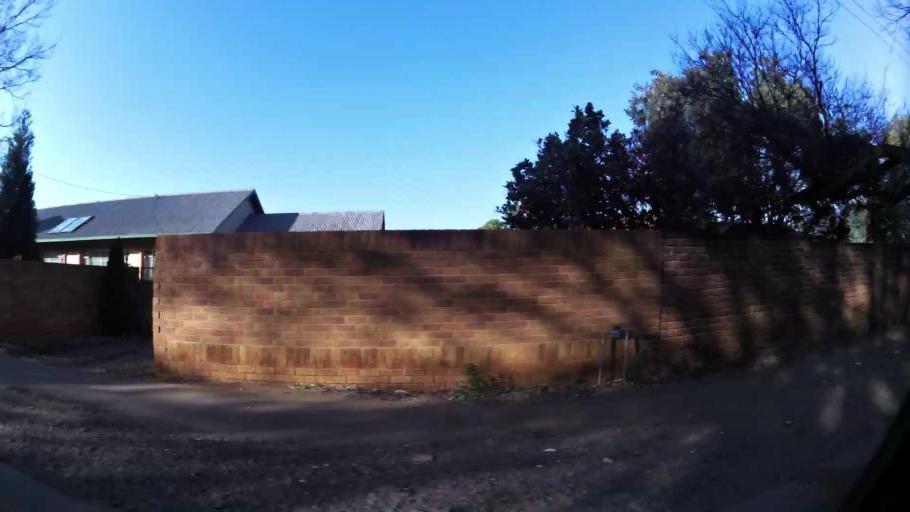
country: ZA
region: Gauteng
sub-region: City of Tshwane Metropolitan Municipality
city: Pretoria
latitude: -25.6995
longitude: 28.1954
